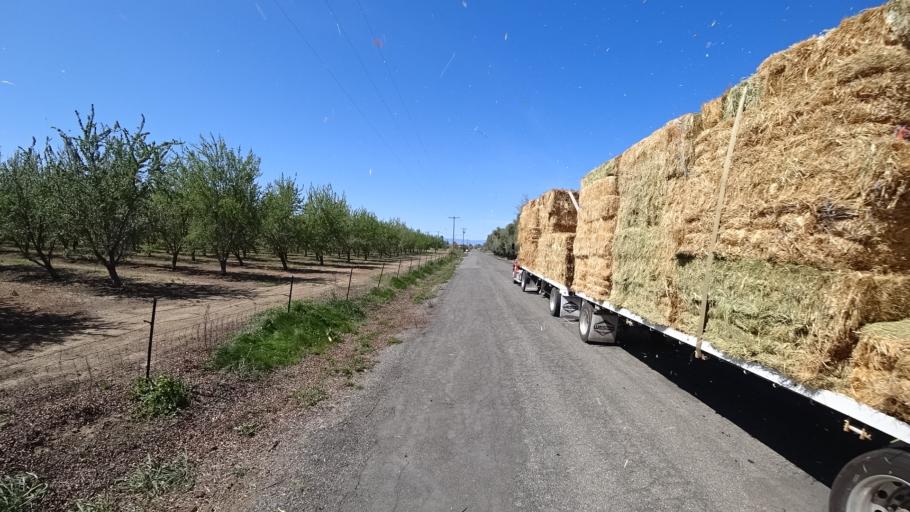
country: US
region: California
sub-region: Glenn County
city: Hamilton City
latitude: 39.7969
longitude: -122.0976
